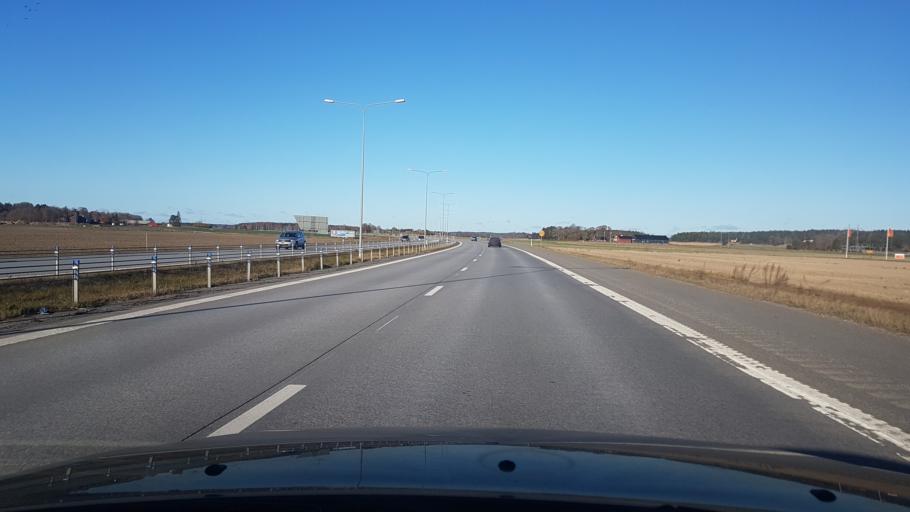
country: SE
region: Uppsala
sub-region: Uppsala Kommun
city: Saevja
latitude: 59.8513
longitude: 17.7338
